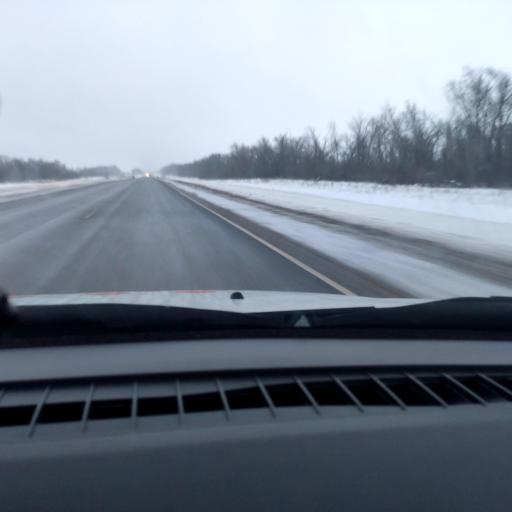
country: RU
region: Samara
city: Dubovyy Umet
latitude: 53.0404
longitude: 50.2084
